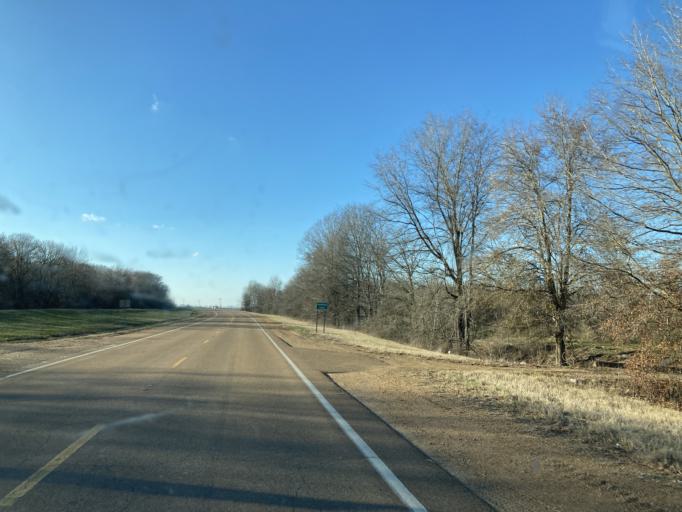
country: US
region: Mississippi
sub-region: Yazoo County
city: Yazoo City
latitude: 32.9230
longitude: -90.5668
